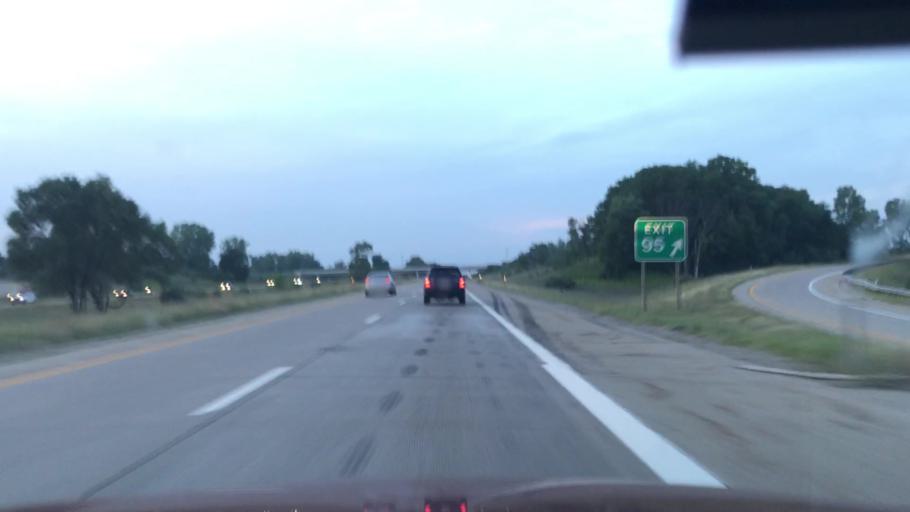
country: US
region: Michigan
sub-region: Kent County
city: Northview
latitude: 43.0849
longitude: -85.6343
